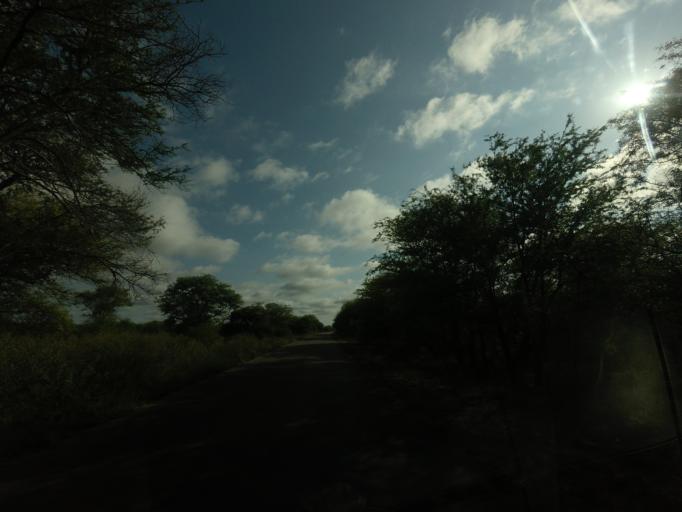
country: ZA
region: Mpumalanga
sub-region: Ehlanzeni District
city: Komatipoort
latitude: -25.2140
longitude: 31.8680
